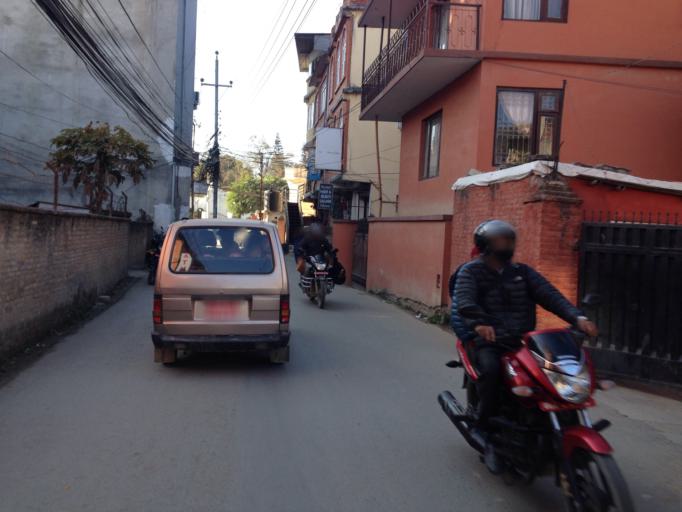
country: NP
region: Central Region
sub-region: Bagmati Zone
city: Kathmandu
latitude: 27.7242
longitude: 85.3317
